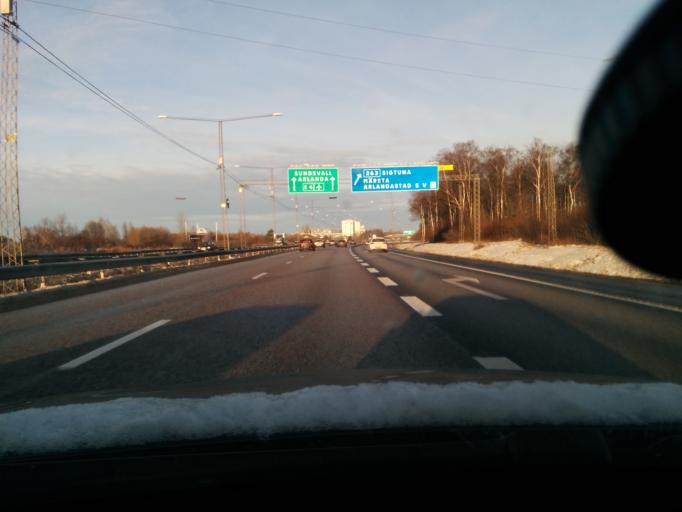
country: SE
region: Stockholm
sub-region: Sigtuna Kommun
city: Rosersberg
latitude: 59.5964
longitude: 17.8965
